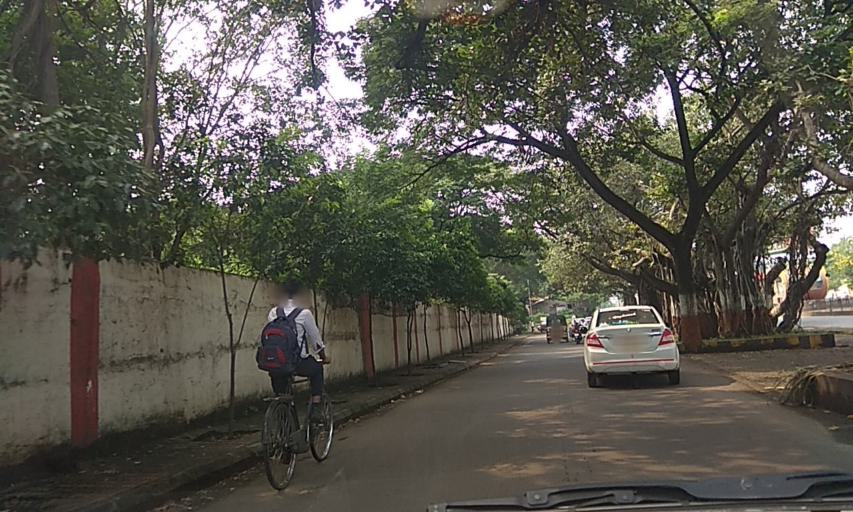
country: IN
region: Maharashtra
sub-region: Pune Division
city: Khadki
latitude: 18.5506
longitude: 73.8725
